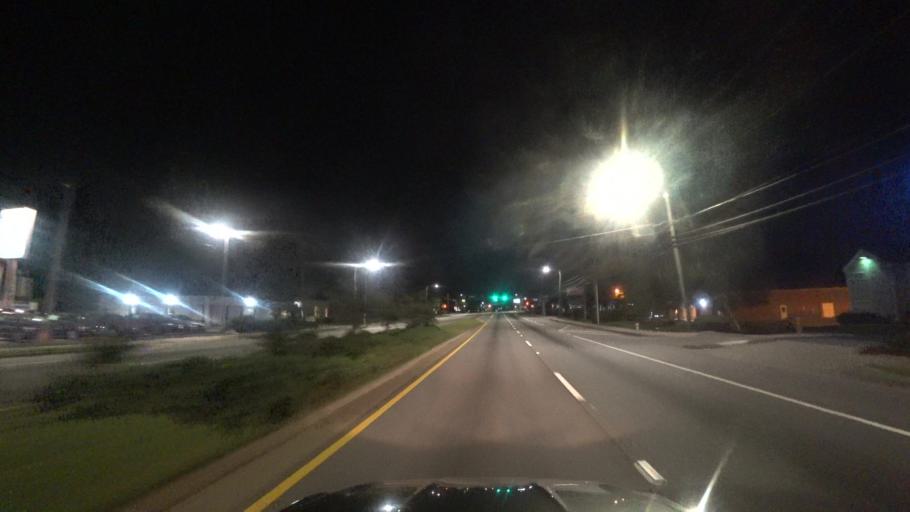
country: US
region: Georgia
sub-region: Clayton County
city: Forest Park
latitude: 33.6207
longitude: -84.3787
